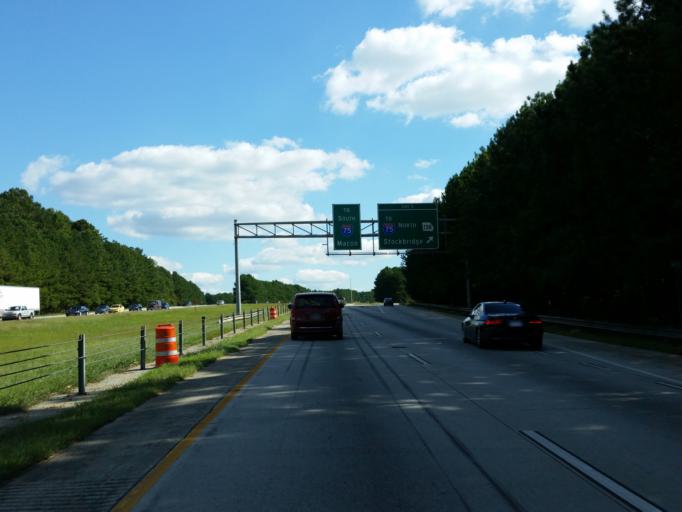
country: US
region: Georgia
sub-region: Henry County
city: Stockbridge
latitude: 33.5584
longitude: -84.2705
